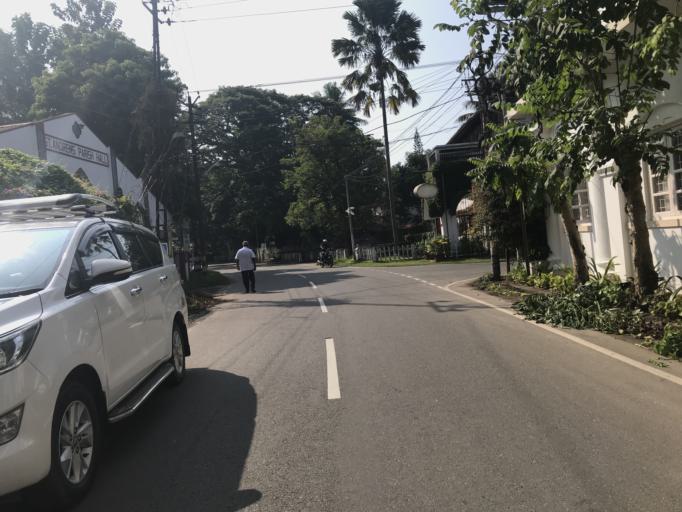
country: IN
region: Kerala
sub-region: Ernakulam
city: Cochin
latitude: 9.9632
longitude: 76.2391
